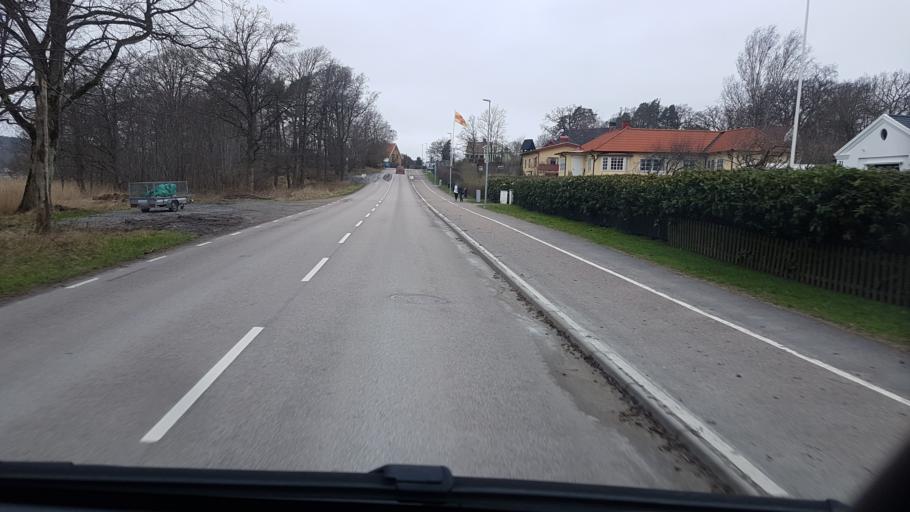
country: SE
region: Vaestra Goetaland
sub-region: Lerums Kommun
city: Lerum
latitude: 57.7703
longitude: 12.2496
